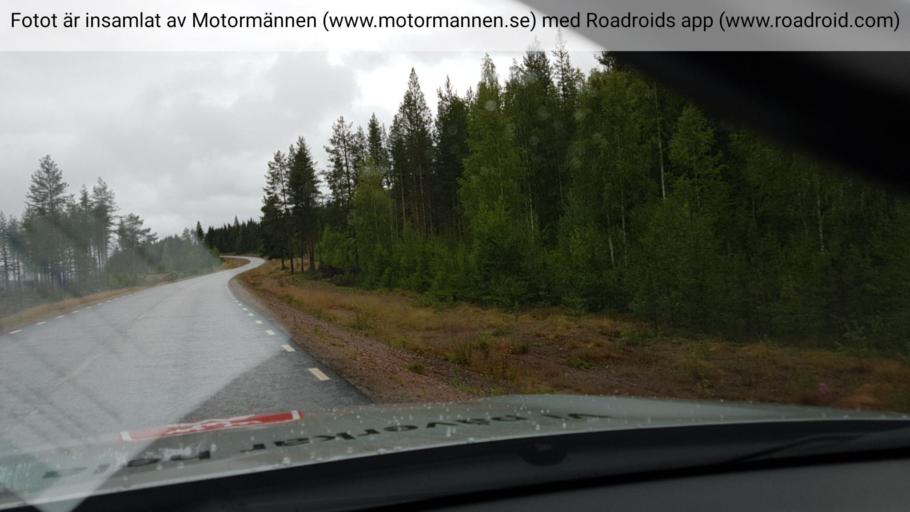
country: SE
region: Norrbotten
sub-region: Gallivare Kommun
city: Gaellivare
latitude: 66.6411
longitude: 20.3961
